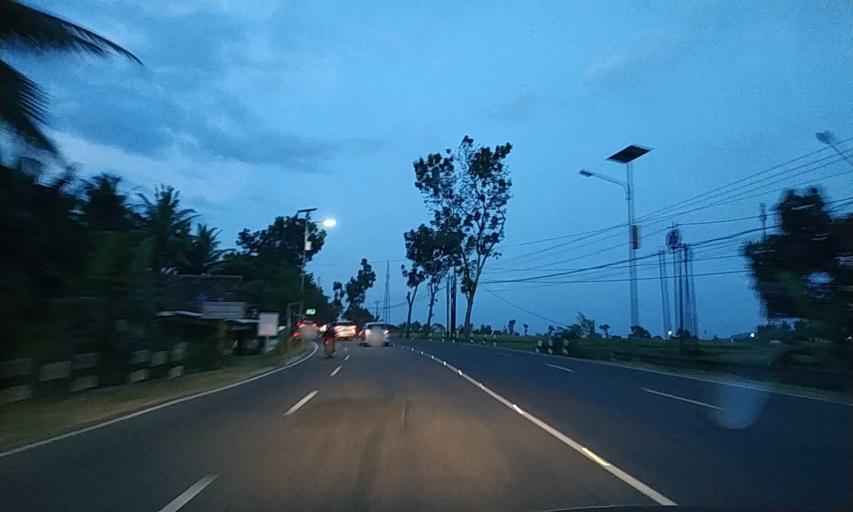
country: ID
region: Daerah Istimewa Yogyakarta
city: Godean
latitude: -7.8151
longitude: 110.2531
